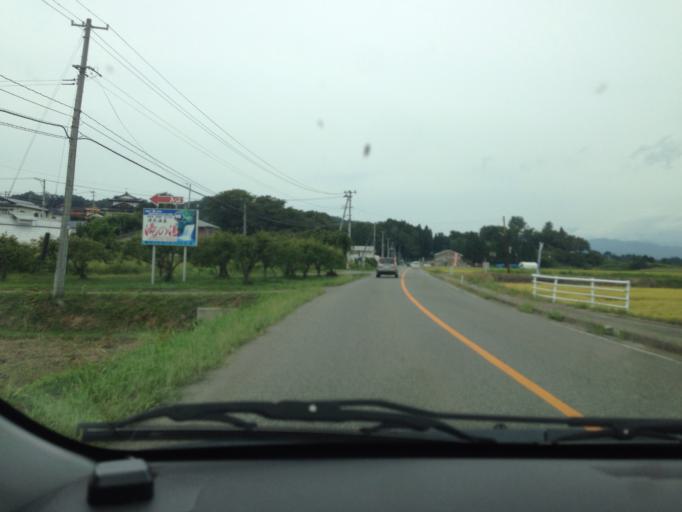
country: JP
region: Fukushima
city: Kitakata
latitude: 37.6070
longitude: 139.8047
